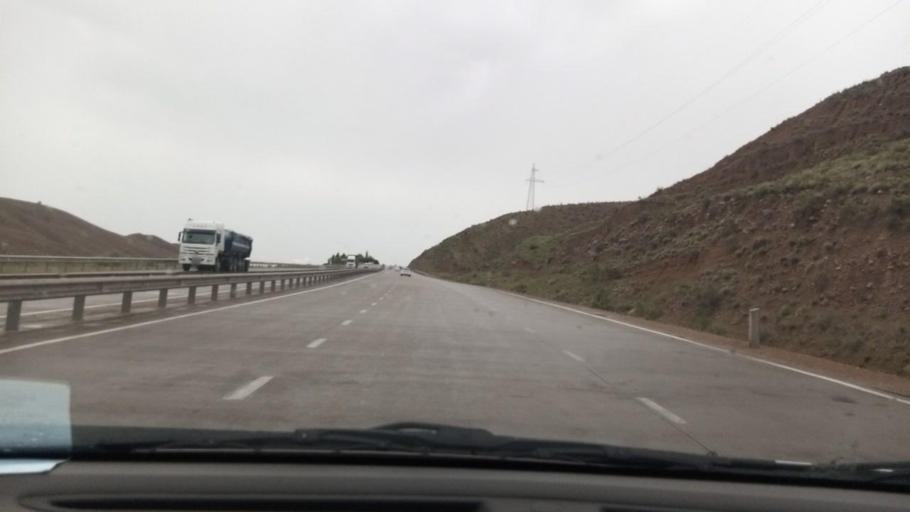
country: UZ
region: Namangan
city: Pop Shahri
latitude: 40.9459
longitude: 70.6832
